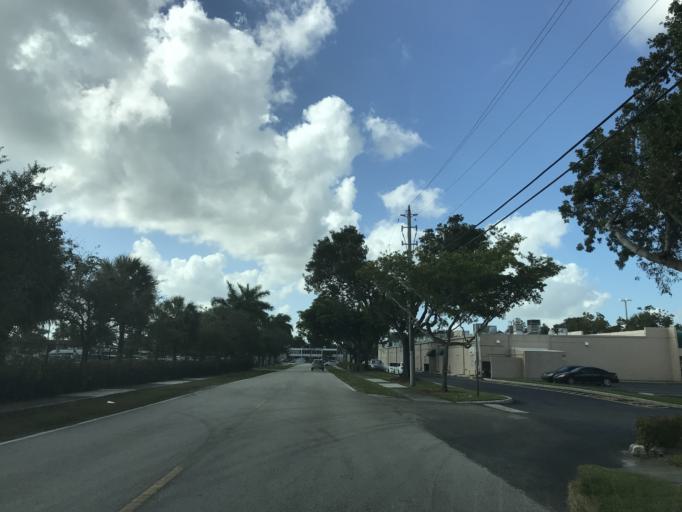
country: US
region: Florida
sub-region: Broward County
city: Margate
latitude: 26.2571
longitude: -80.1994
